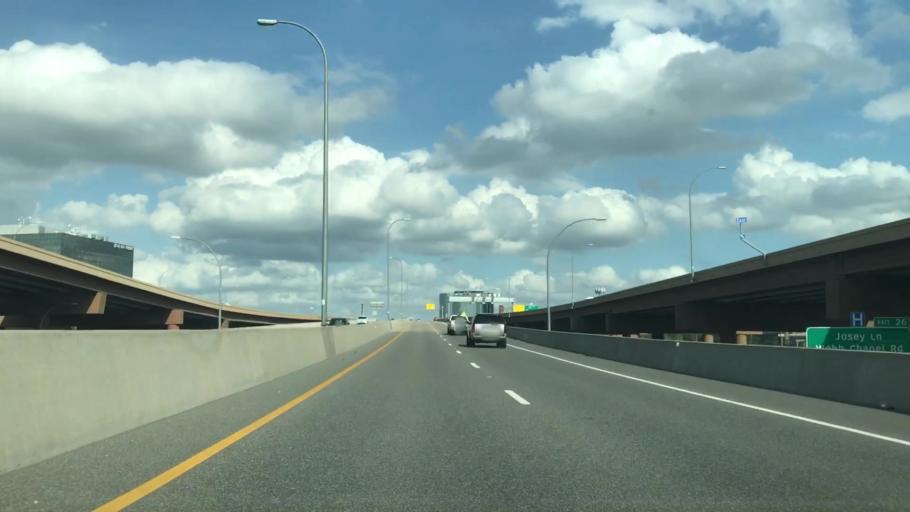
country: US
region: Texas
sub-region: Dallas County
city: Farmers Branch
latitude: 32.9094
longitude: -96.8888
